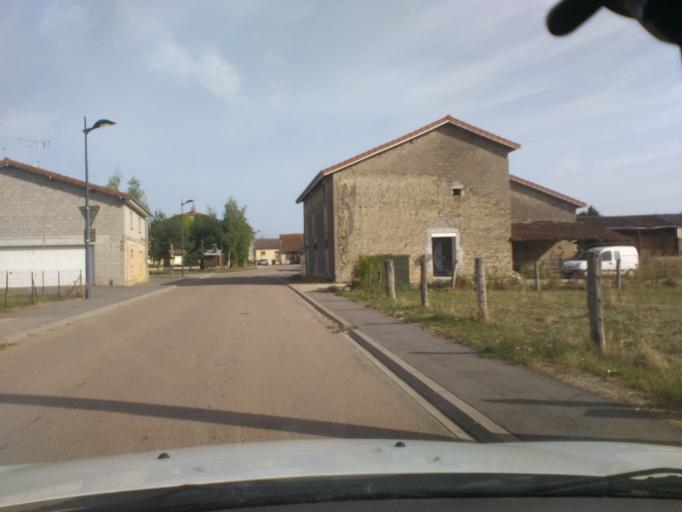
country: FR
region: Lorraine
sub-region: Departement des Vosges
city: Mirecourt
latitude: 48.3336
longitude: 6.0979
